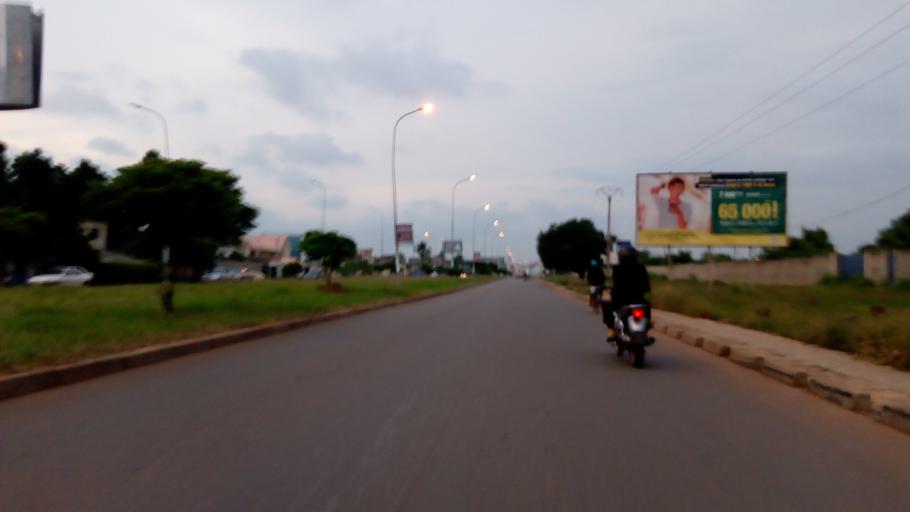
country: TG
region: Maritime
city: Lome
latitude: 6.2079
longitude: 1.1939
